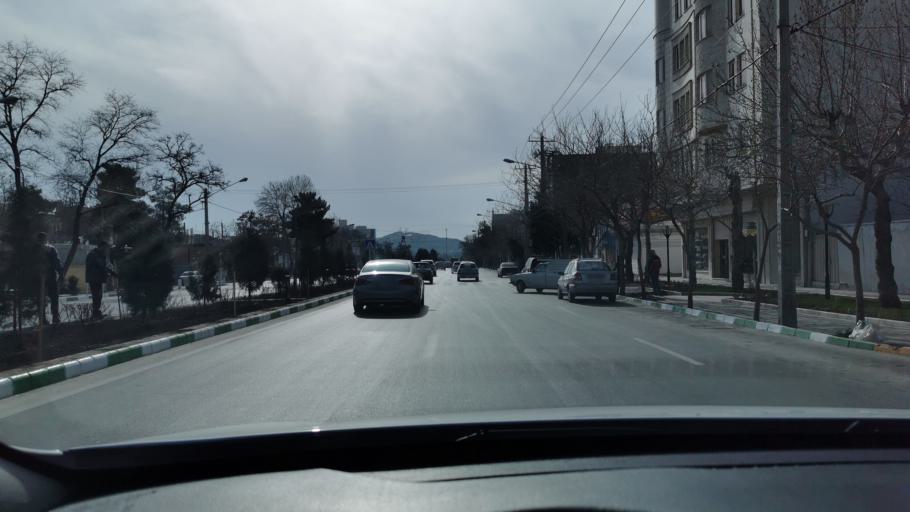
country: IR
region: Razavi Khorasan
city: Mashhad
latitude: 36.2868
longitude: 59.5448
